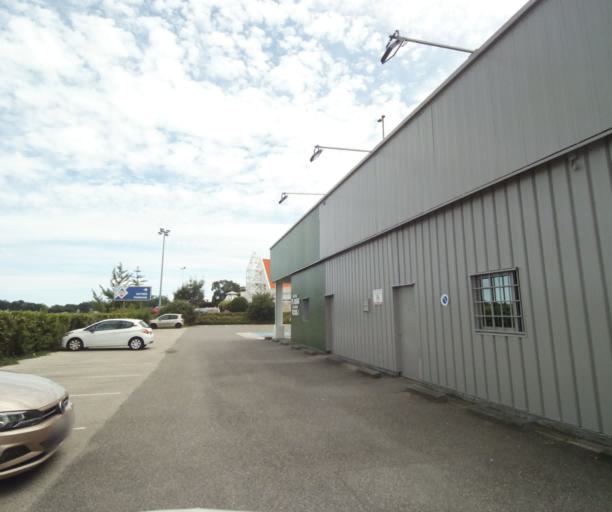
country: FR
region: Rhone-Alpes
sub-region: Departement de la Haute-Savoie
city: Anthy-sur-Leman
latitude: 46.3457
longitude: 6.4211
